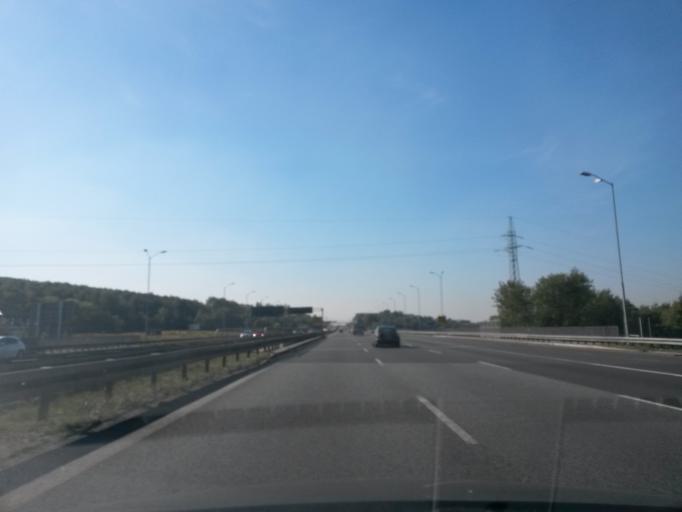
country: PL
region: Silesian Voivodeship
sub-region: Swietochlowice
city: Swietochlowice
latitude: 50.2533
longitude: 18.9346
